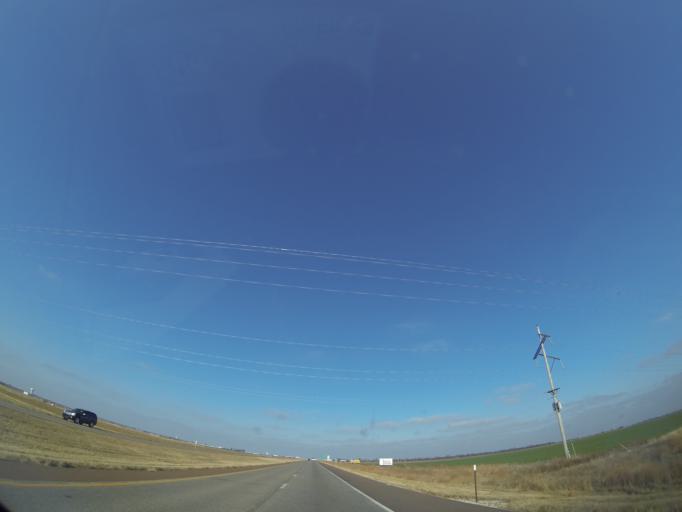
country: US
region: Kansas
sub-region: McPherson County
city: McPherson
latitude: 38.3479
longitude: -97.6208
